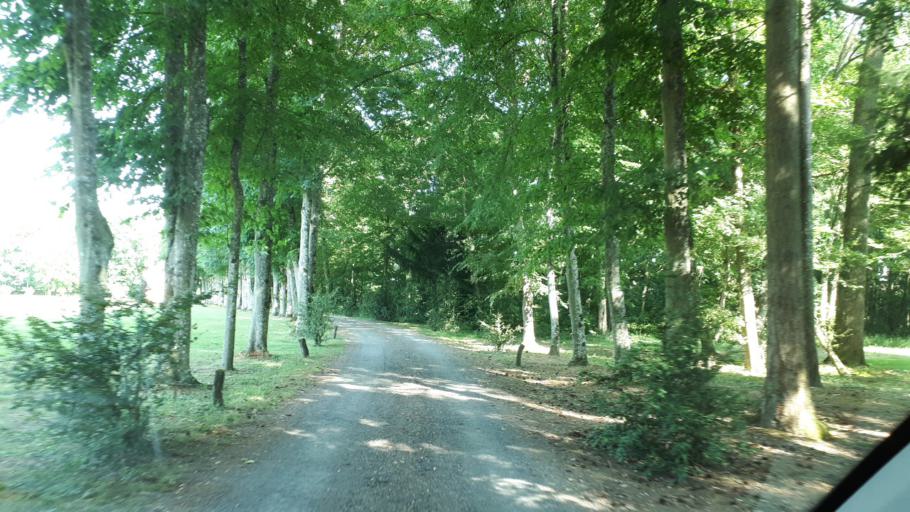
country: FR
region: Centre
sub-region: Departement d'Eure-et-Loir
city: Arrou
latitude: 48.0819
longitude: 1.1381
